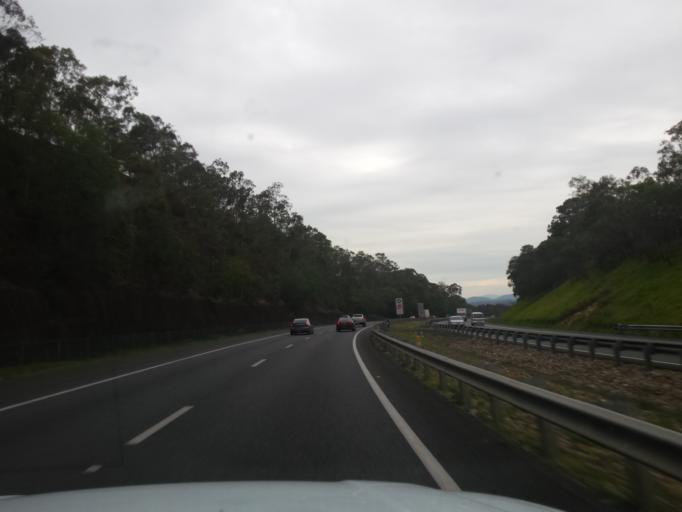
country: AU
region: Queensland
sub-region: Logan
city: Slacks Creek
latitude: -27.6695
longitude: 153.1653
